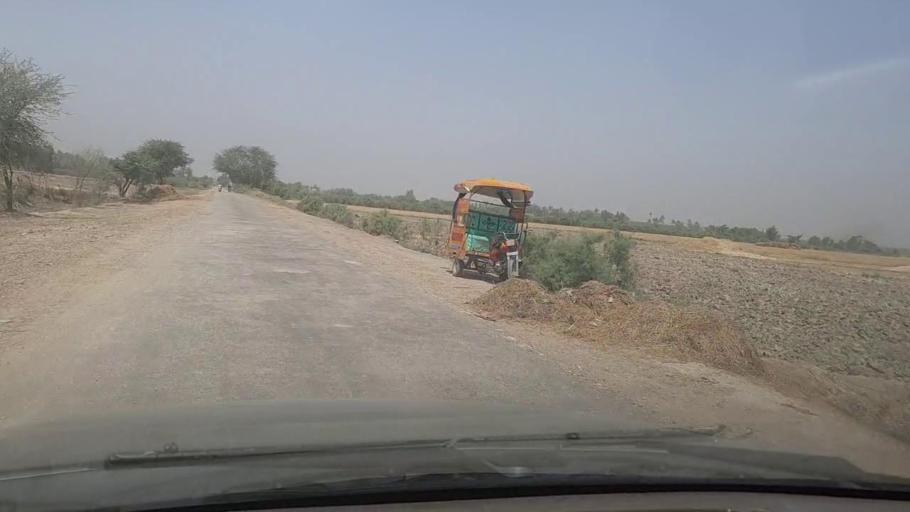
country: PK
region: Sindh
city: Madeji
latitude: 27.7976
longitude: 68.4315
